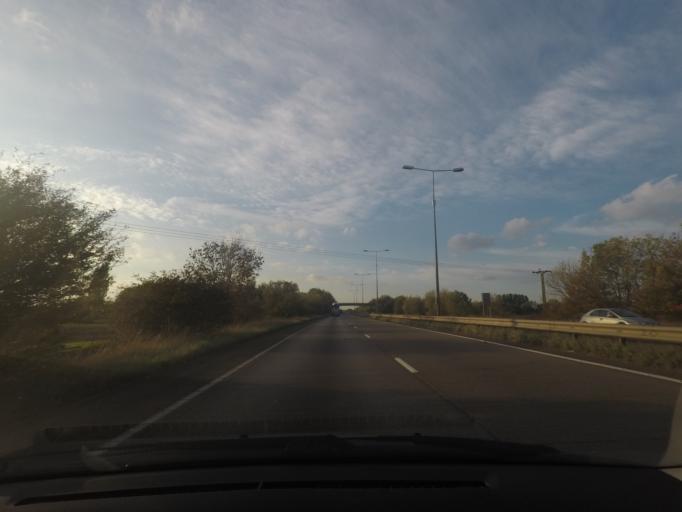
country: GB
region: England
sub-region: North East Lincolnshire
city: Healing
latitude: 53.5873
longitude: -0.1544
